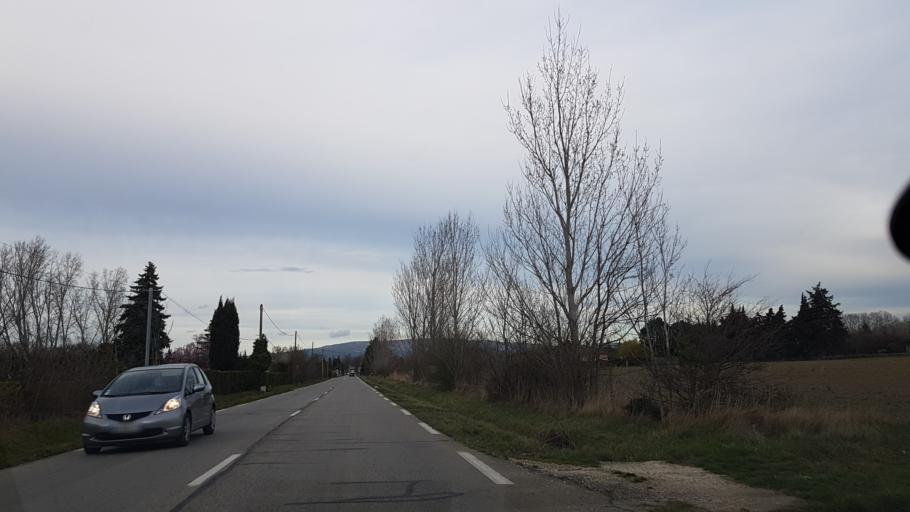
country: FR
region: Provence-Alpes-Cote d'Azur
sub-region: Departement du Vaucluse
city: Le Thor
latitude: 43.9243
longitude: 4.9745
